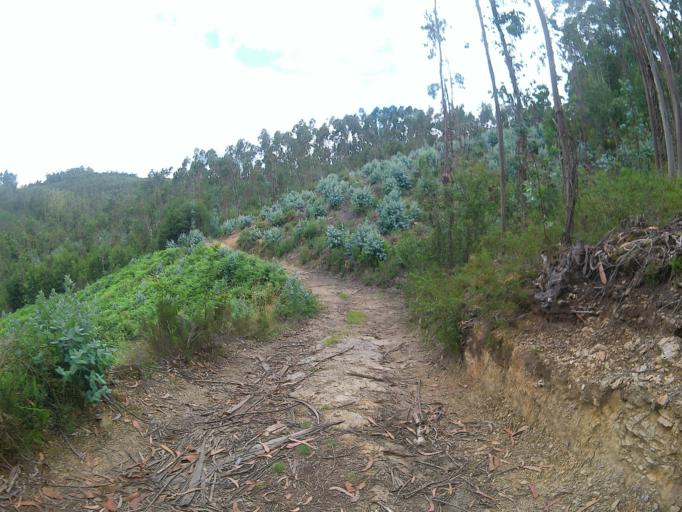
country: PT
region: Aveiro
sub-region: Albergaria-A-Velha
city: Branca
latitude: 40.7699
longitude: -8.4359
